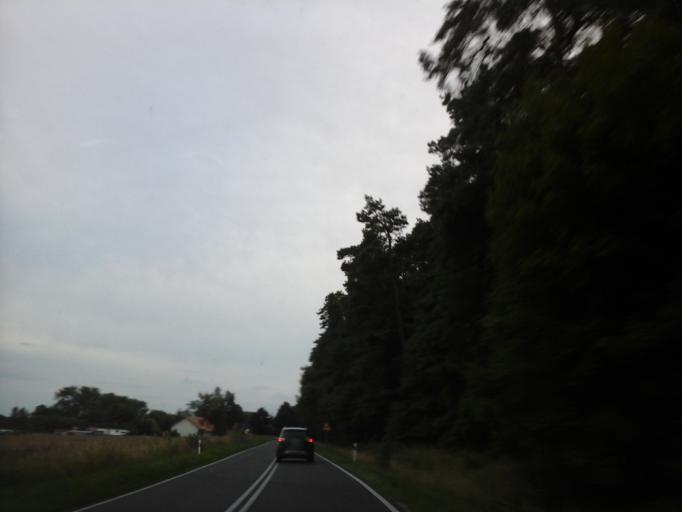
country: PL
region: West Pomeranian Voivodeship
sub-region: Powiat stargardzki
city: Stara Dabrowa
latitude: 53.4047
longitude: 15.0994
